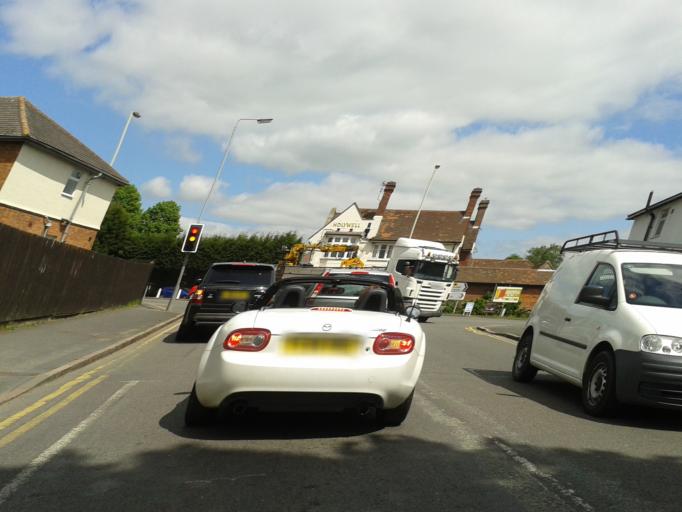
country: GB
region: England
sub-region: Leicestershire
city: Hinckley
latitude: 52.5404
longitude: -1.3594
